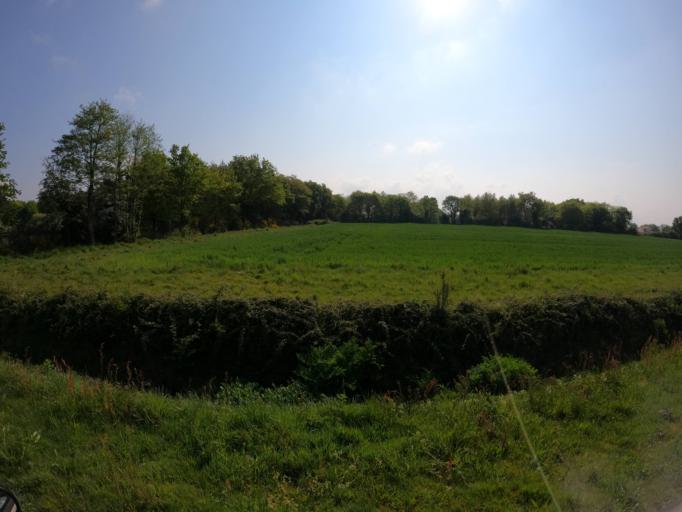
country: FR
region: Pays de la Loire
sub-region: Departement de la Vendee
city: Treize-Septiers
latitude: 47.0016
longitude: -1.2426
